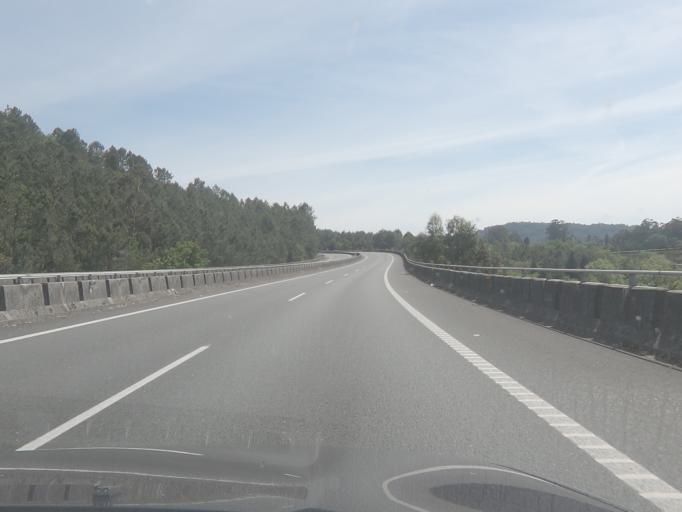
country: ES
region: Galicia
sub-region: Provincia de Pontevedra
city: Portas
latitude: 42.5870
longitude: -8.6757
